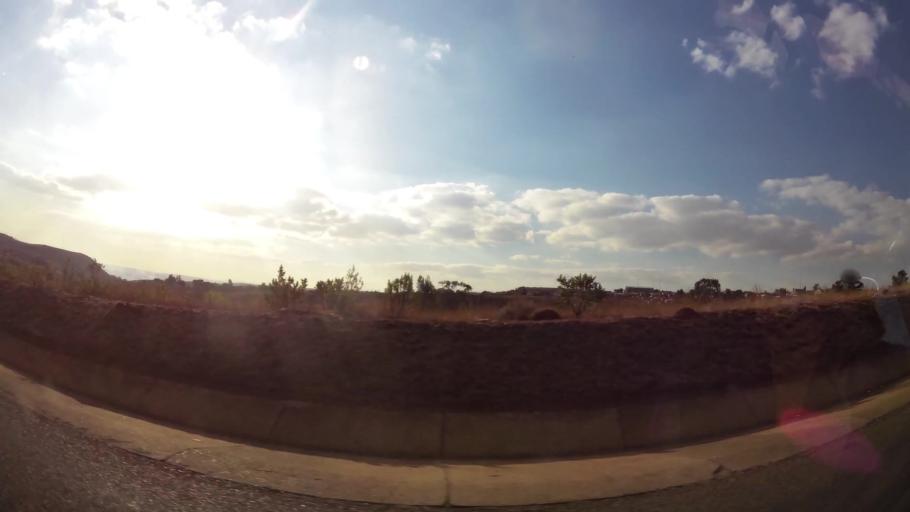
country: ZA
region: Gauteng
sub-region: West Rand District Municipality
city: Krugersdorp
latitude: -26.0852
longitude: 27.7506
